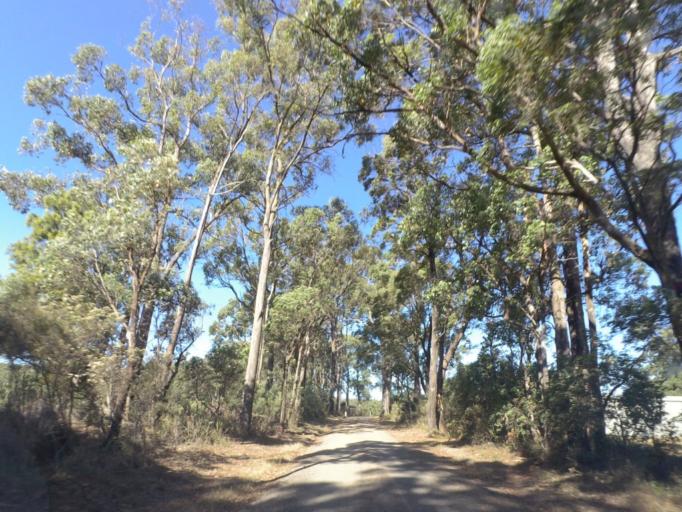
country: AU
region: Victoria
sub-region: Murrindindi
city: Kinglake West
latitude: -37.4773
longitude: 145.3385
